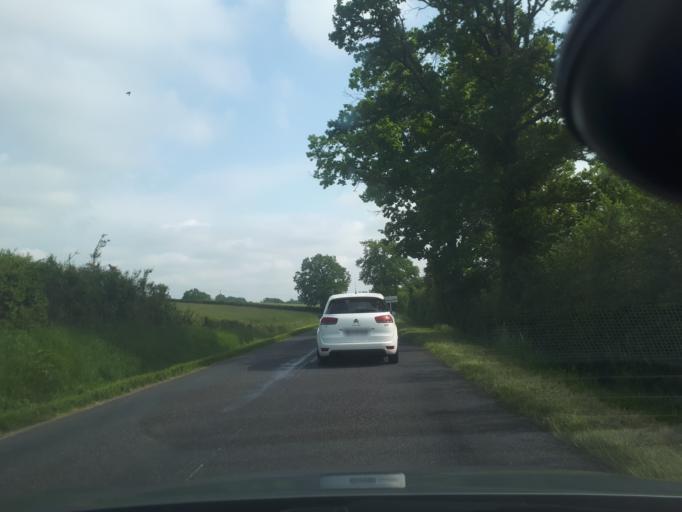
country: FR
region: Auvergne
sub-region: Departement de l'Allier
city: Saint-Gerand-le-Puy
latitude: 46.3656
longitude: 3.5794
